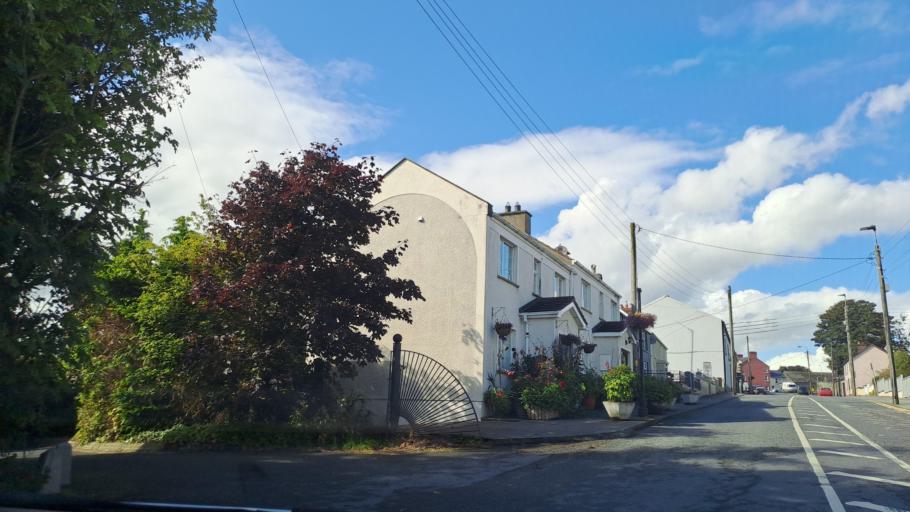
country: IE
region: Ulster
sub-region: An Cabhan
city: Bailieborough
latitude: 53.9928
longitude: -6.8940
